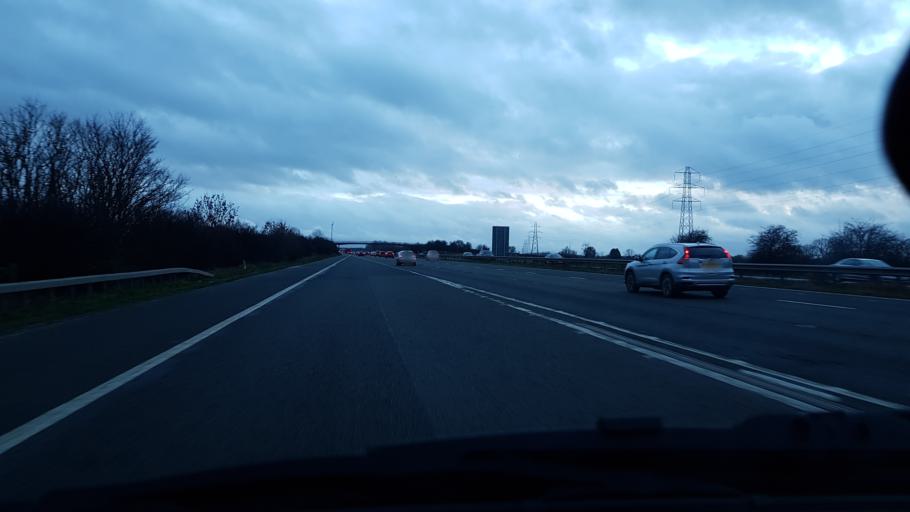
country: GB
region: England
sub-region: Gloucestershire
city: Tewkesbury
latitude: 51.9930
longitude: -2.1239
